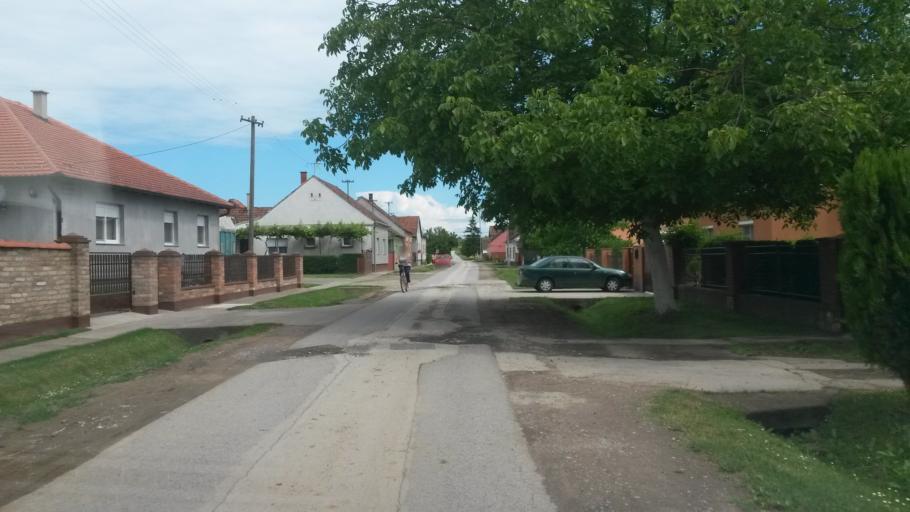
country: HR
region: Vukovarsko-Srijemska
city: Vodinci
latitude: 45.2777
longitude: 18.6107
